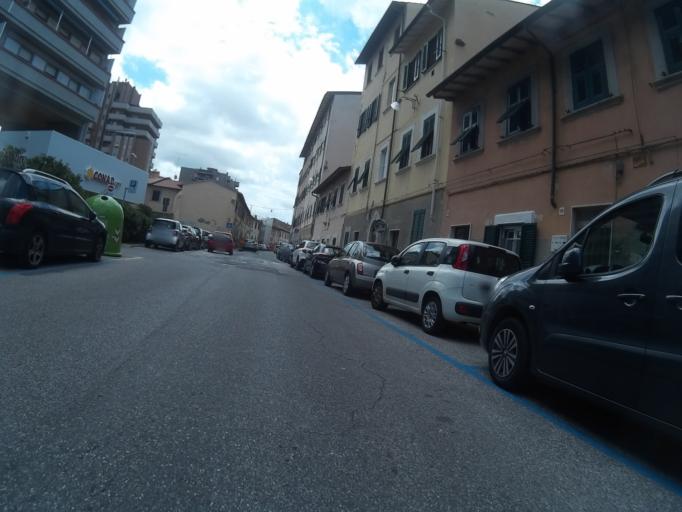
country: IT
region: Tuscany
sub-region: Provincia di Livorno
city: Livorno
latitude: 43.5396
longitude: 10.3045
